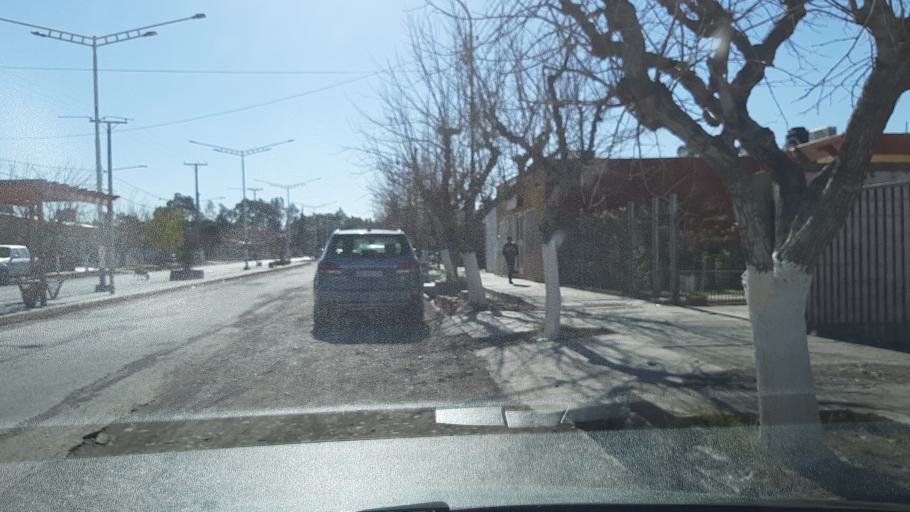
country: AR
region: San Juan
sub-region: Departamento de Zonda
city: Zonda
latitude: -31.5479
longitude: -68.7318
